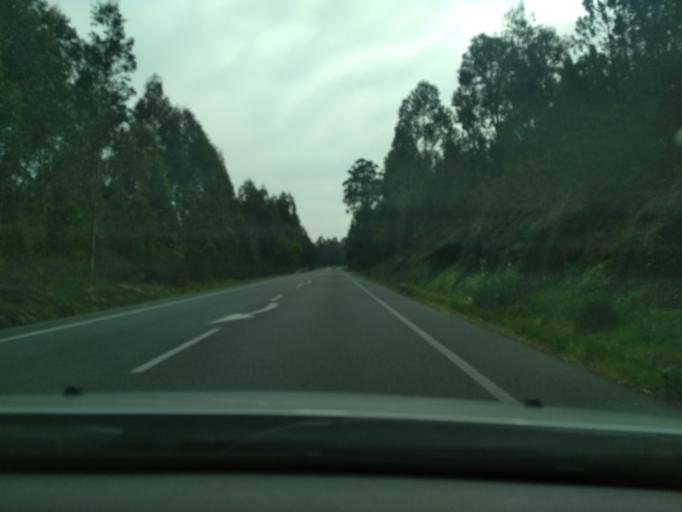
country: ES
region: Galicia
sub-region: Provincia de Pontevedra
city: Catoira
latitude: 42.6530
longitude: -8.7015
